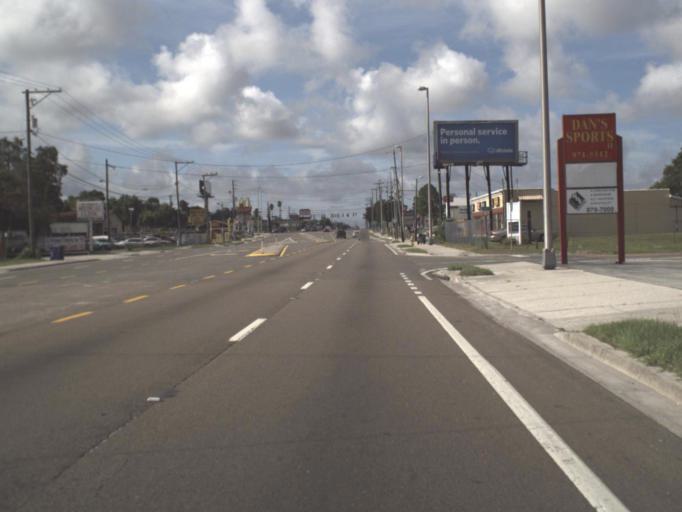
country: US
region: Florida
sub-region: Hillsborough County
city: University
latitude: 28.0580
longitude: -82.4513
